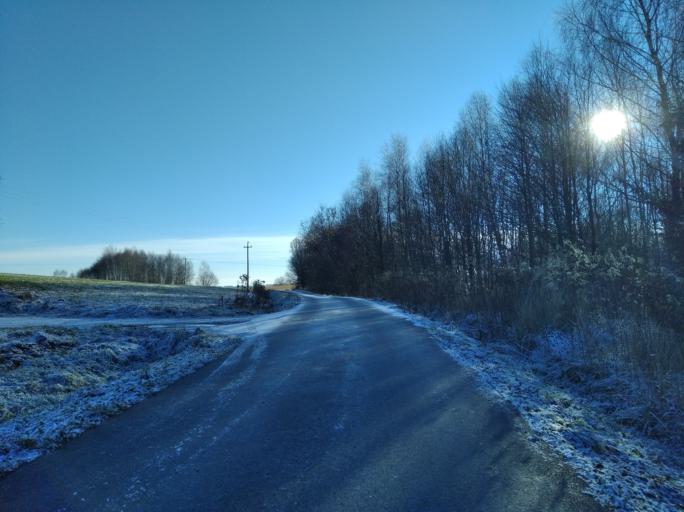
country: PL
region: Subcarpathian Voivodeship
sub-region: Powiat strzyzowski
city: Czudec
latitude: 49.9454
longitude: 21.7661
